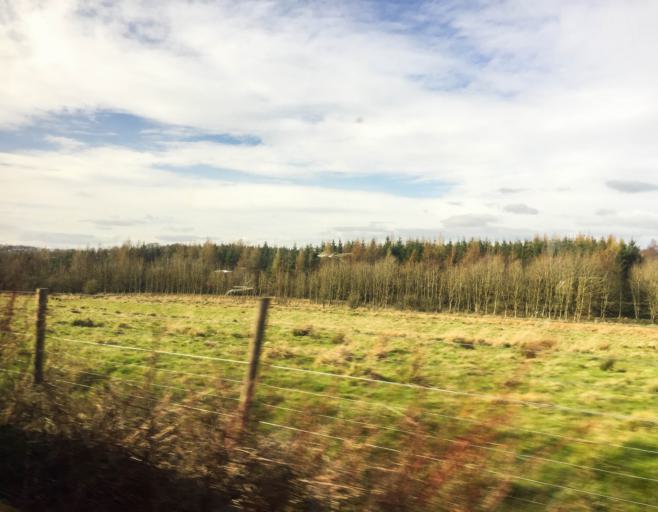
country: GB
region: Scotland
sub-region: North Lanarkshire
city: Stepps
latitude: 55.8892
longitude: -4.1605
